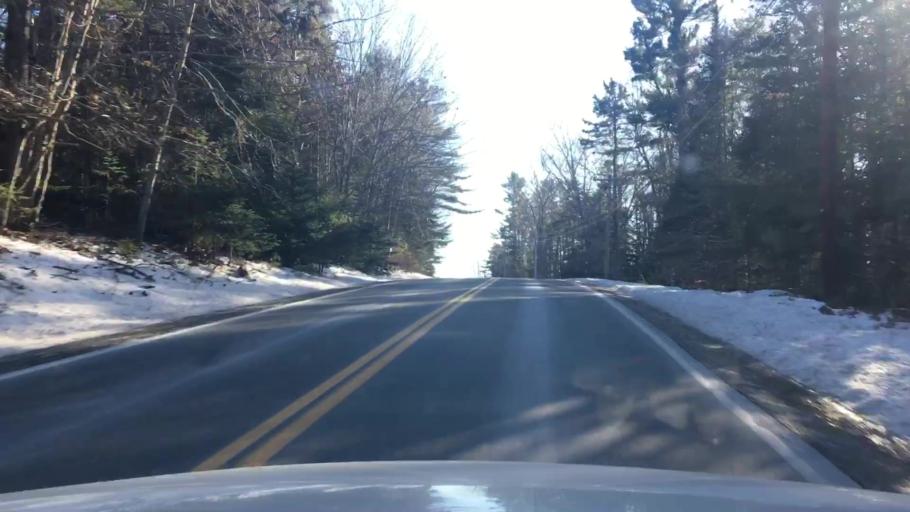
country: US
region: Maine
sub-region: Hancock County
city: Orland
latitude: 44.5370
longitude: -68.7463
